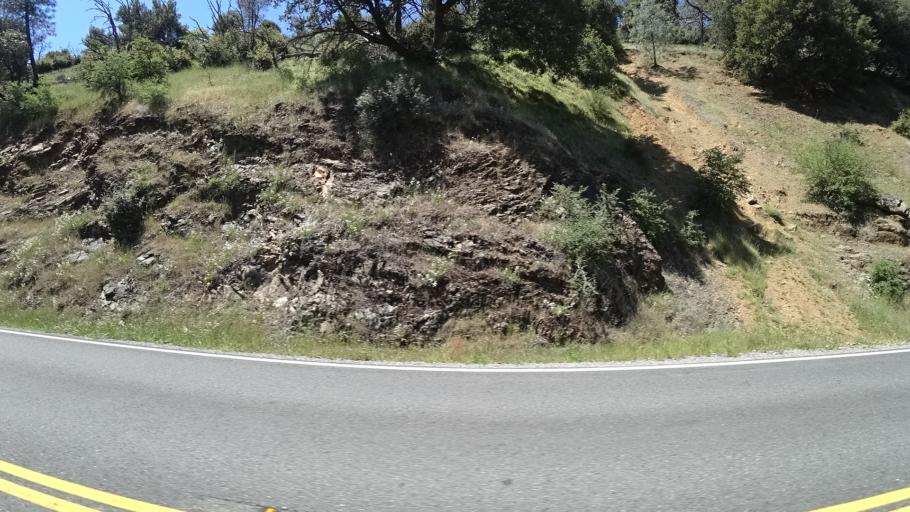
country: US
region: California
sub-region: Trinity County
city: Weaverville
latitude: 40.7382
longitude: -123.0067
